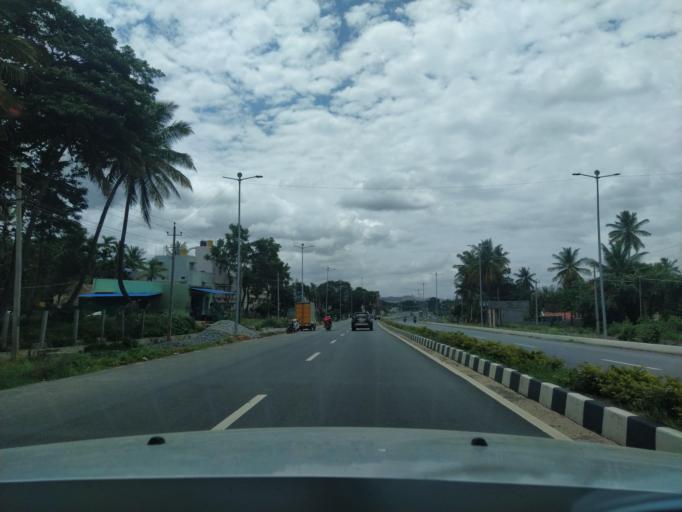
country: IN
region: Karnataka
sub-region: Tumkur
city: Tumkur
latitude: 13.3086
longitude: 77.1444
